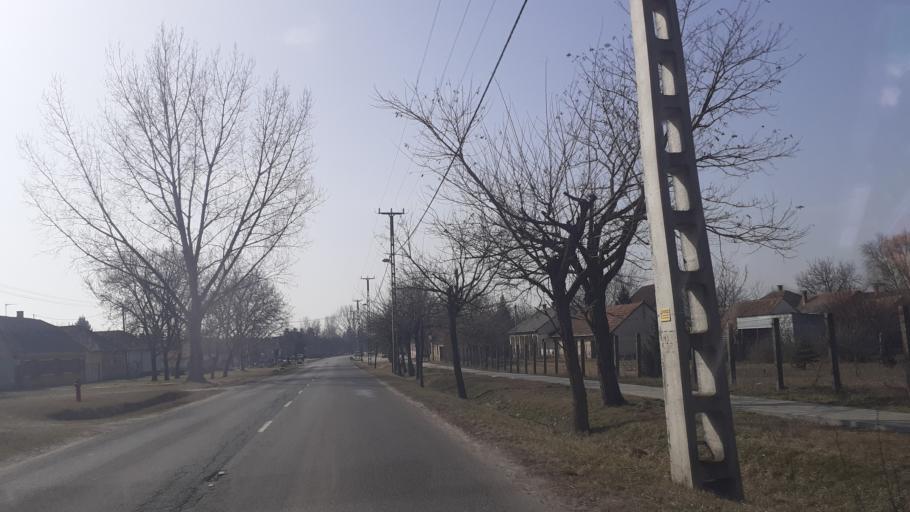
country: HU
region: Pest
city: Orkeny
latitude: 47.0839
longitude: 19.3736
